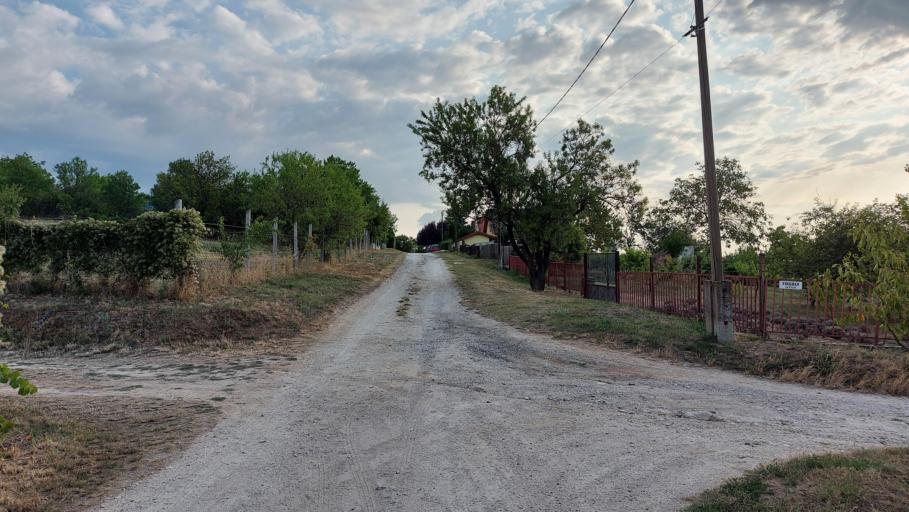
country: HU
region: Veszprem
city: Balatonalmadi
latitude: 47.0531
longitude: 18.0053
